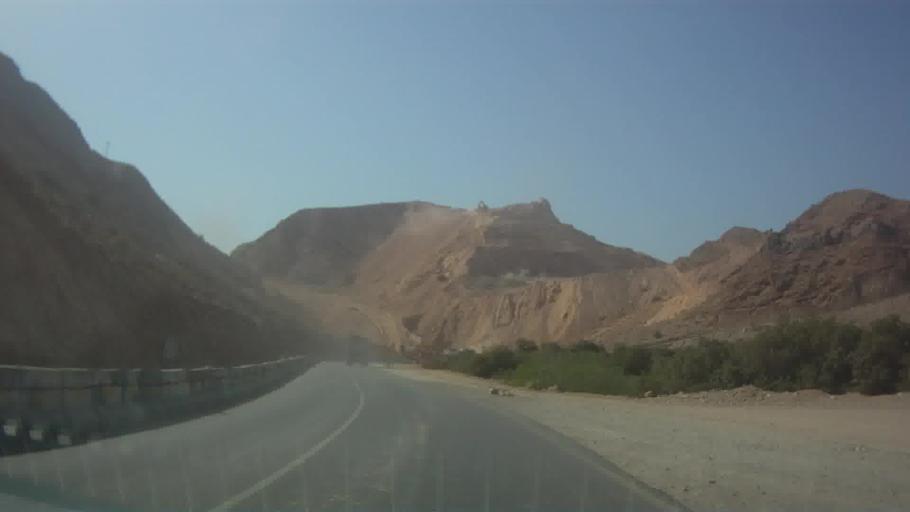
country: OM
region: Muhafazat Masqat
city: Muscat
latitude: 23.5100
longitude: 58.7237
